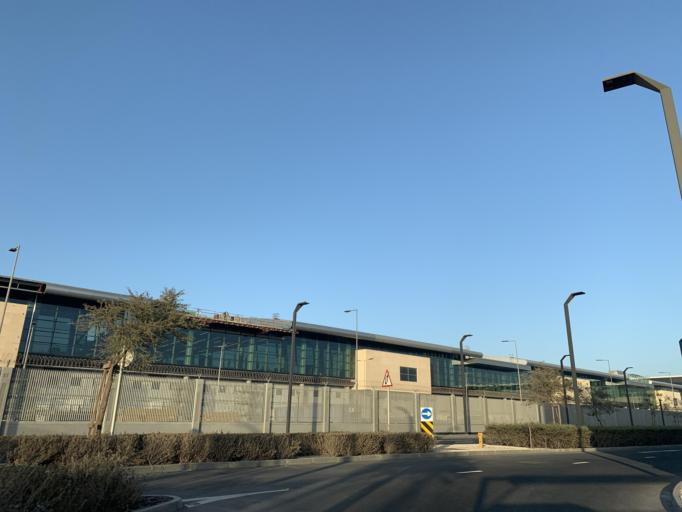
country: BH
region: Muharraq
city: Al Muharraq
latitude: 26.2684
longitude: 50.6268
